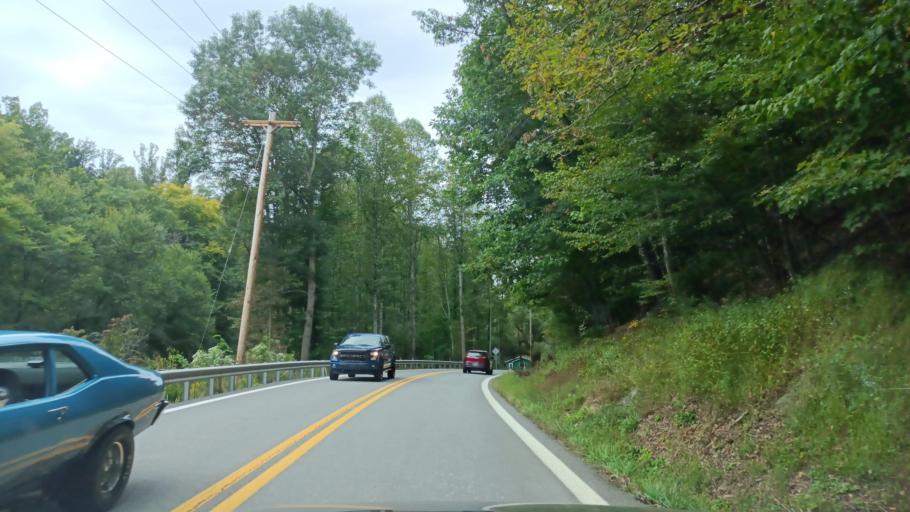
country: US
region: West Virginia
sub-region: Taylor County
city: Grafton
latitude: 39.3292
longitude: -79.9117
